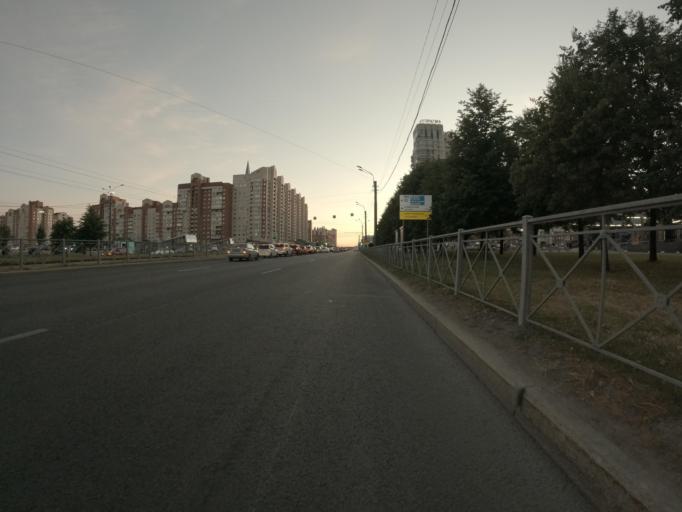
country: RU
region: Leningrad
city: Untolovo
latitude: 59.9886
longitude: 30.2055
